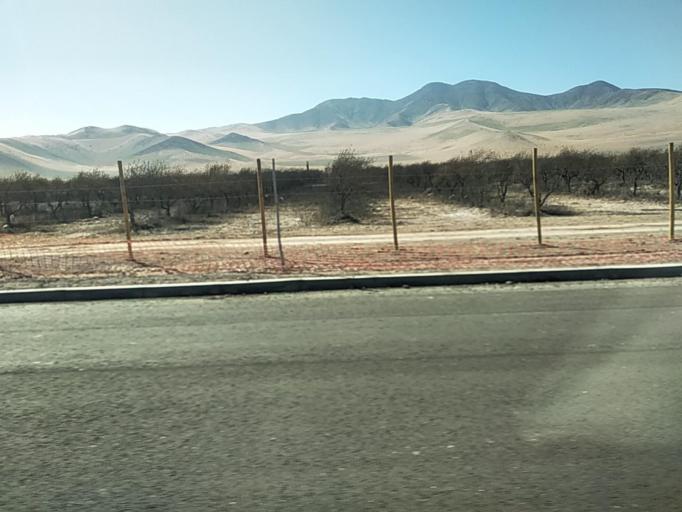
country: CL
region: Atacama
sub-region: Provincia de Copiapo
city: Copiapo
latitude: -27.3329
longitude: -70.5792
